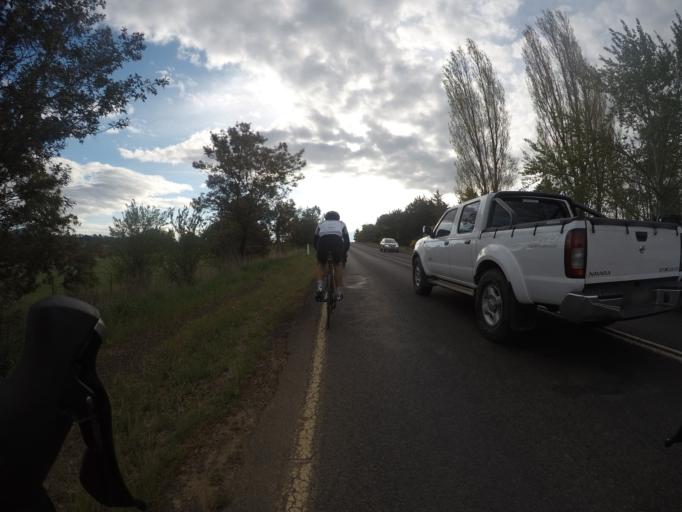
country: AU
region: New South Wales
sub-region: Orange Municipality
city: Orange
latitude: -33.2891
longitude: 149.0313
